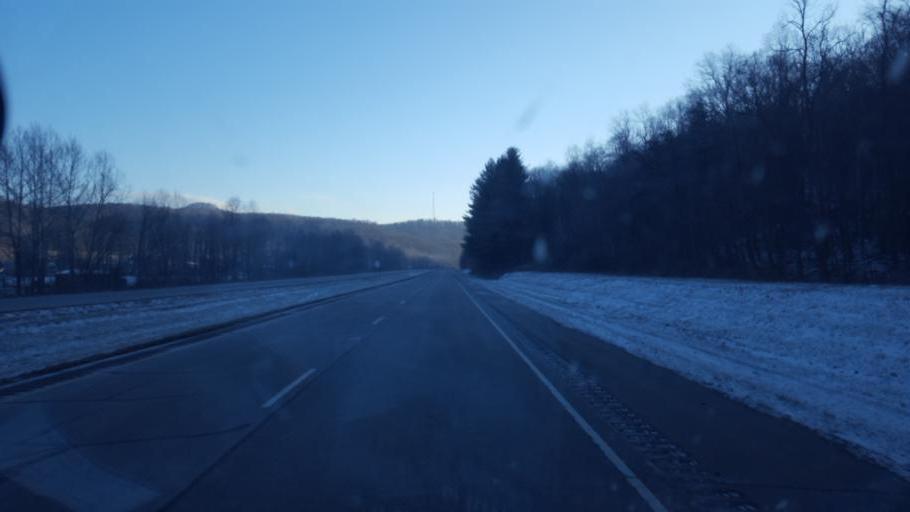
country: US
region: Ohio
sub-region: Pike County
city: Piketon
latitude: 39.0602
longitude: -83.0921
